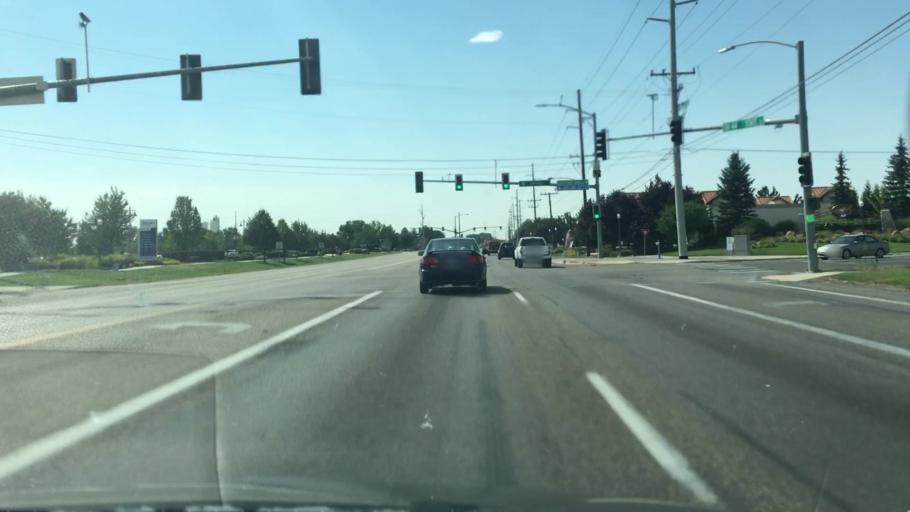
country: US
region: Idaho
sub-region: Ada County
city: Eagle
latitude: 43.6825
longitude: -116.3137
